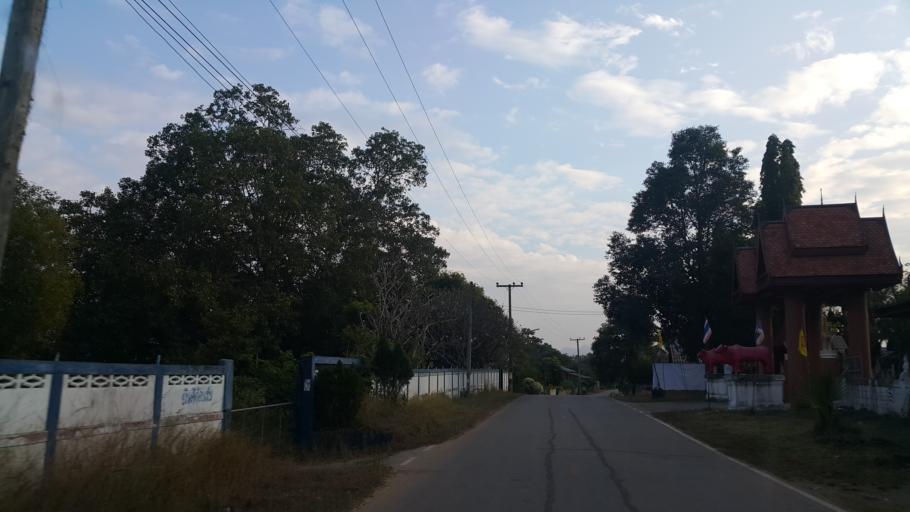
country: TH
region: Lampang
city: Sop Prap
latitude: 17.9065
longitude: 99.3298
